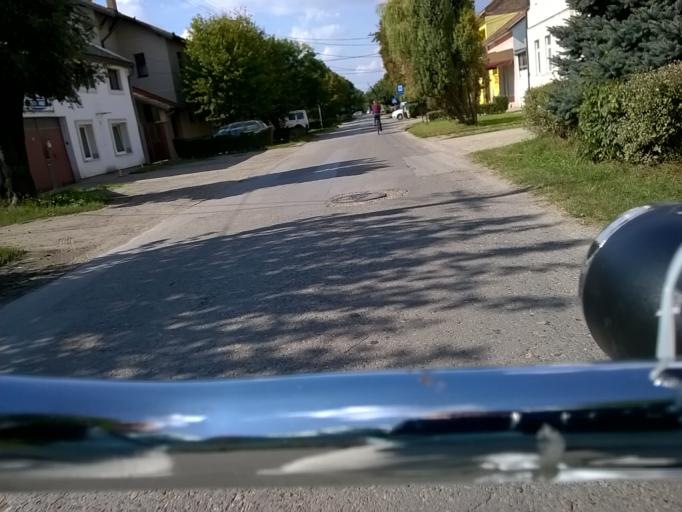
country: RS
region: Autonomna Pokrajina Vojvodina
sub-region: Juznobanatski Okrug
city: Pancevo
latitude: 44.8767
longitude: 20.6379
